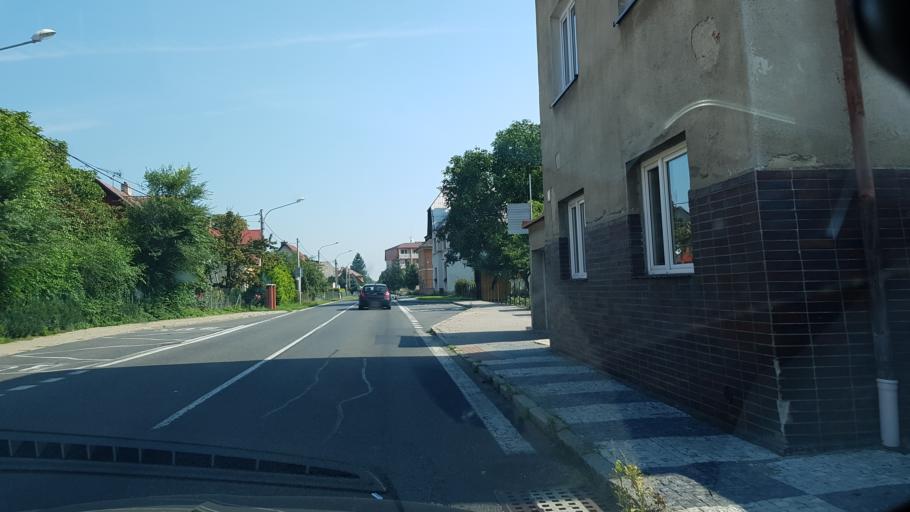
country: CZ
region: Olomoucky
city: Ceska Ves
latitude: 50.2514
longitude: 17.2217
